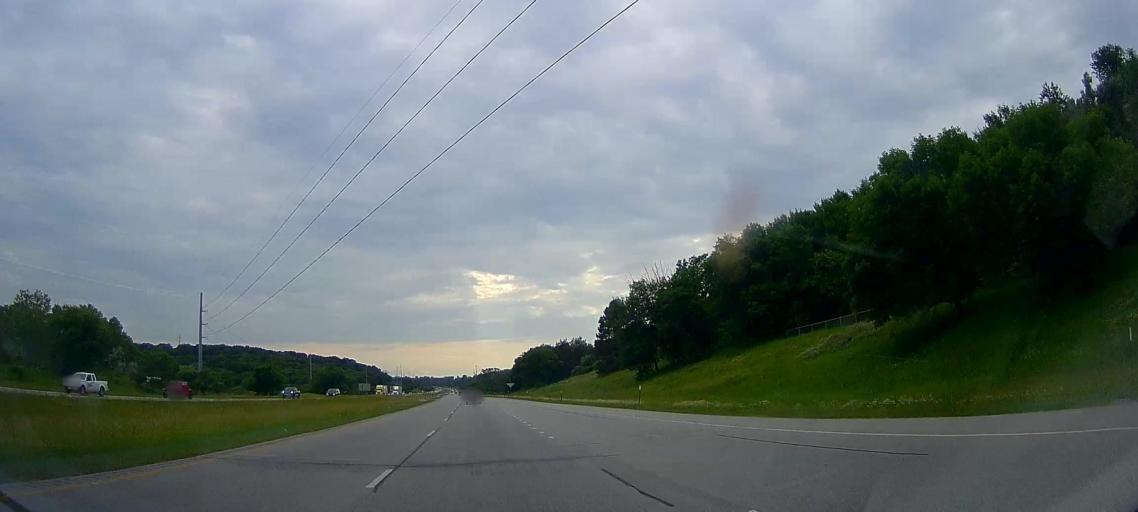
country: US
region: Iowa
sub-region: Pottawattamie County
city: Carter Lake
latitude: 41.3474
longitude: -95.9893
